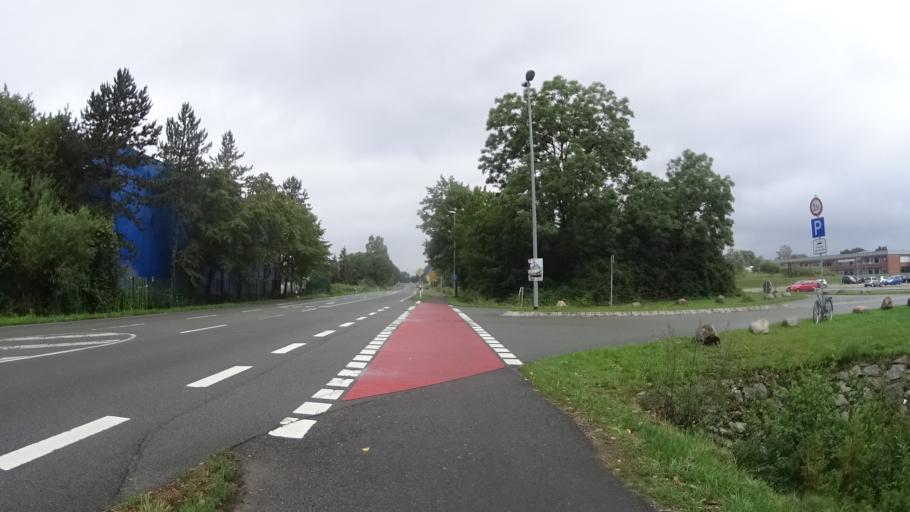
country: DE
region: Lower Saxony
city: Leer
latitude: 53.2250
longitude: 7.4364
